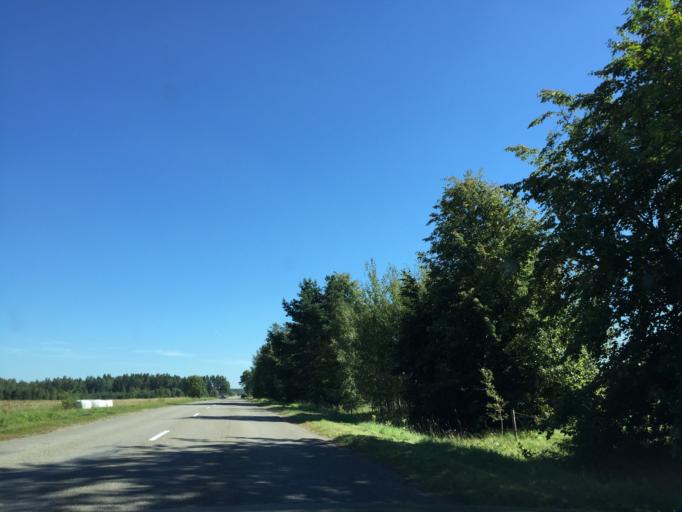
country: LV
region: Akniste
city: Akniste
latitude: 56.1493
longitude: 25.7831
